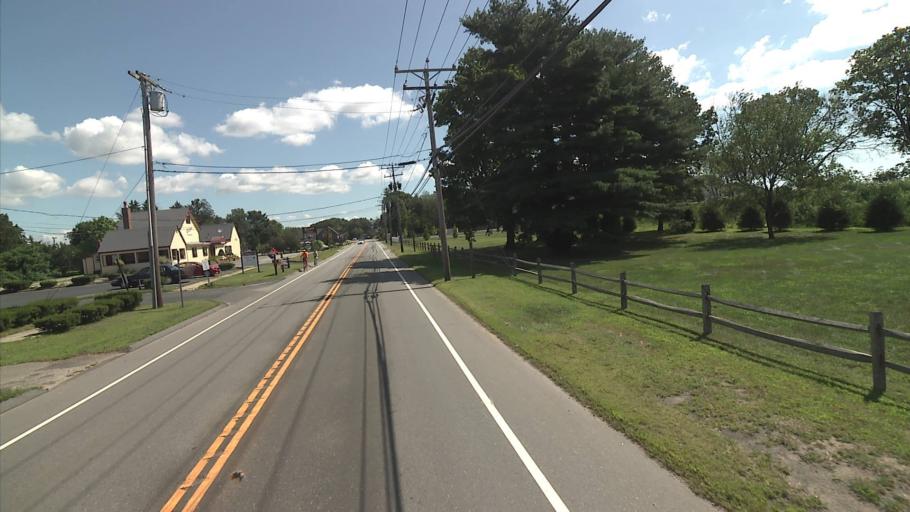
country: US
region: Connecticut
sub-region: Middlesex County
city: Westbrook Center
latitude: 41.2786
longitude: -72.4641
